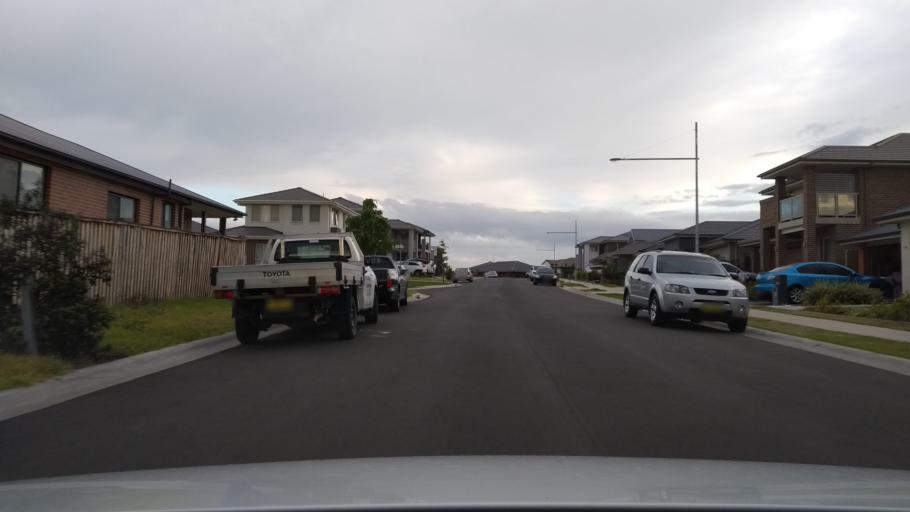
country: AU
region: New South Wales
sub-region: Camden
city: Narellan
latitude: -34.0010
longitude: 150.7294
